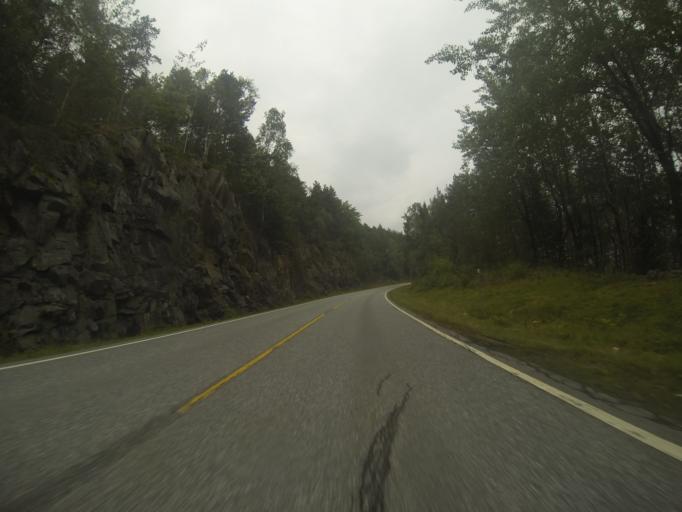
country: NO
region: Rogaland
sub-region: Suldal
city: Sand
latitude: 59.5167
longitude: 6.2301
